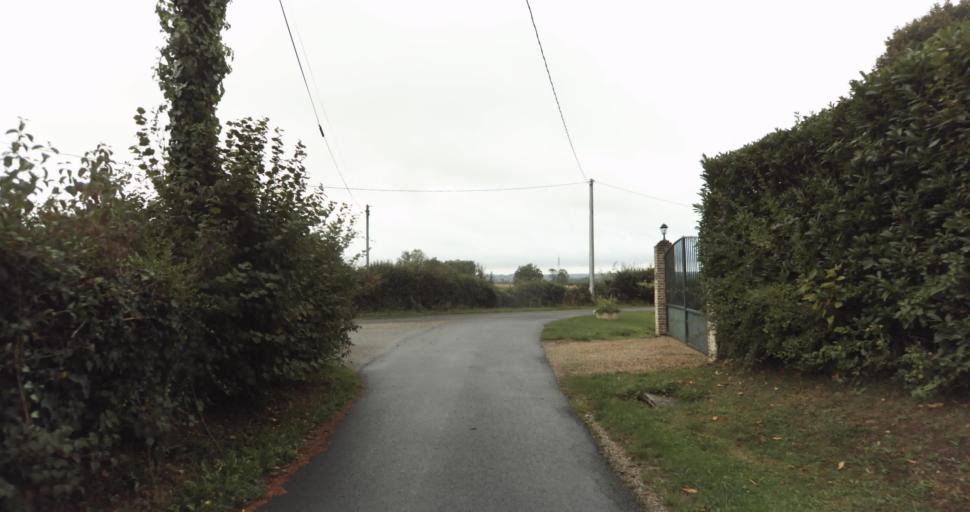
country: FR
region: Lower Normandy
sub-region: Departement de l'Orne
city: Sainte-Gauburge-Sainte-Colombe
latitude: 48.7474
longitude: 0.4214
